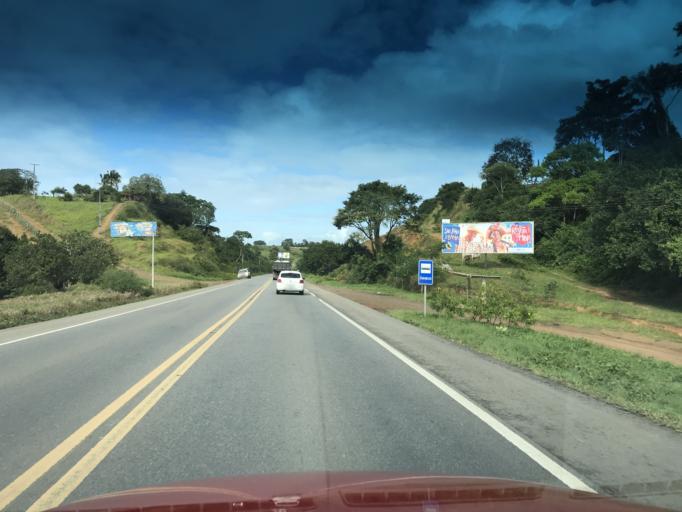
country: BR
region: Bahia
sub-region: Conceicao Do Almeida
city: Muritiba
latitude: -12.9039
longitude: -39.2375
